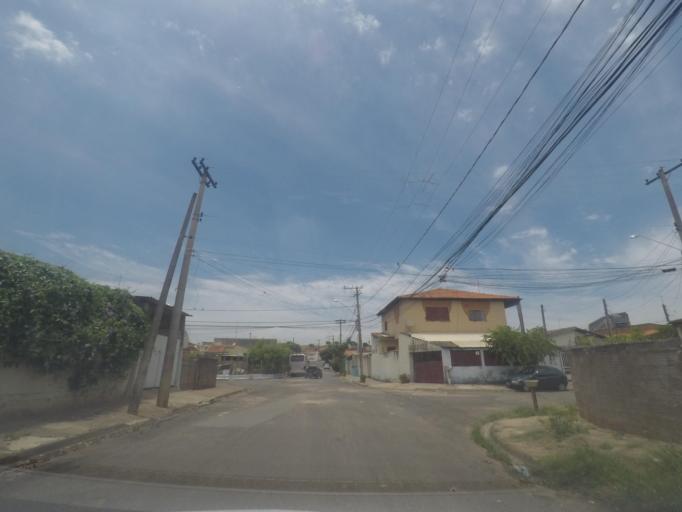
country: BR
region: Sao Paulo
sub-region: Nova Odessa
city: Nova Odessa
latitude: -22.7911
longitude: -47.2795
